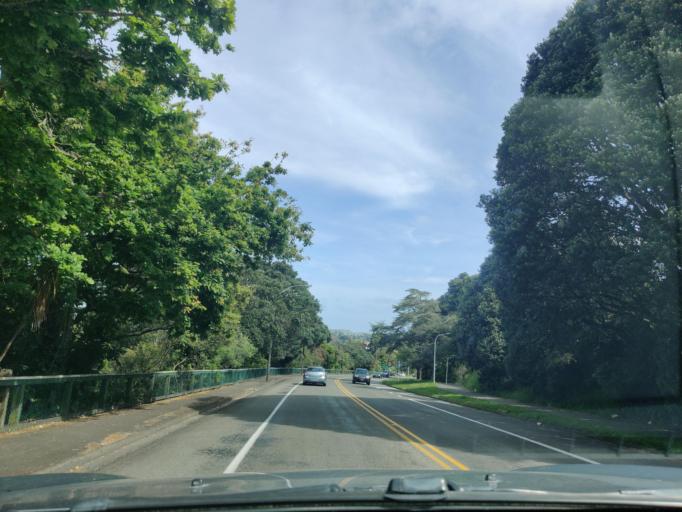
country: NZ
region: Manawatu-Wanganui
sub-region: Wanganui District
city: Wanganui
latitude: -39.9204
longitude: 175.0390
